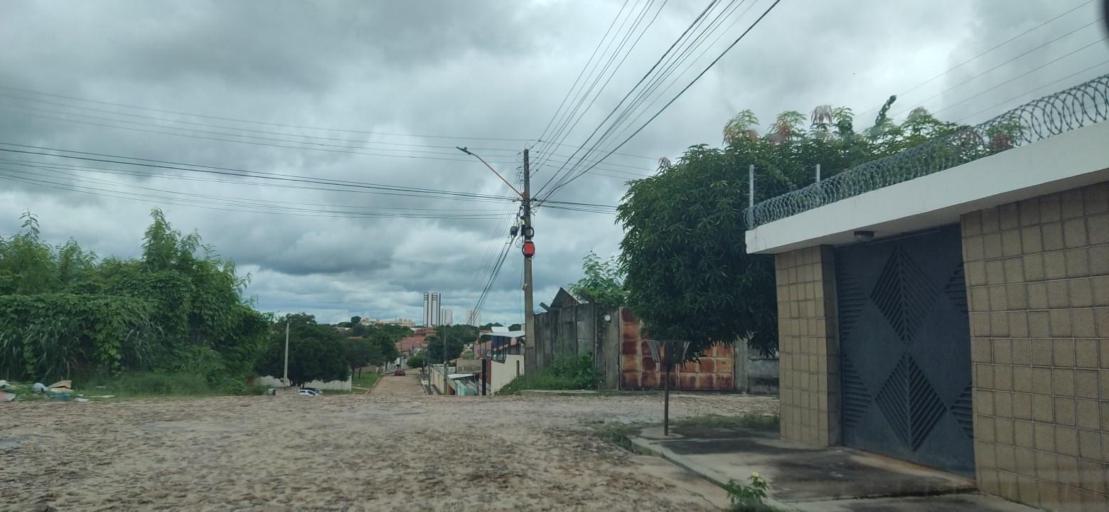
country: BR
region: Piaui
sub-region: Teresina
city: Teresina
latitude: -5.0712
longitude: -42.7595
